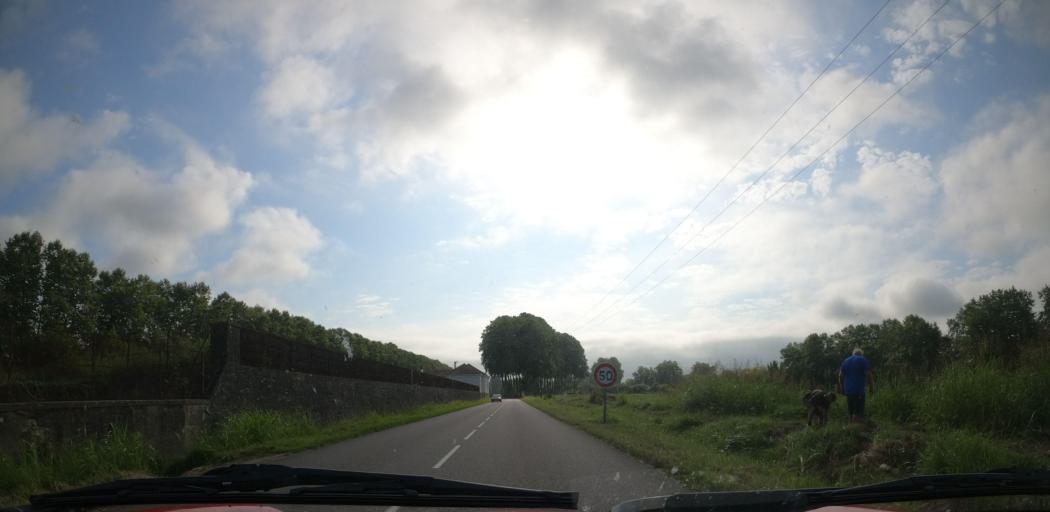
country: FR
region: Aquitaine
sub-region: Departement des Landes
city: Peyrehorade
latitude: 43.5418
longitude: -1.0936
